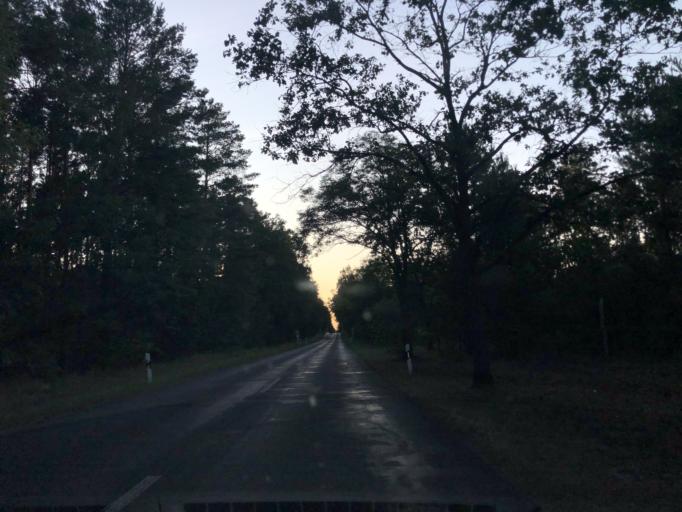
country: DE
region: Brandenburg
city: Mullrose
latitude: 52.2493
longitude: 14.4439
